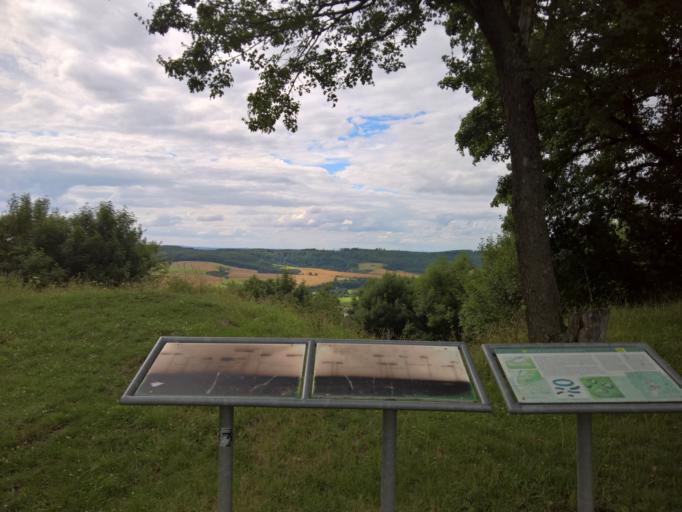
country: DE
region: Hesse
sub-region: Regierungsbezirk Darmstadt
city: Glauburg
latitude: 50.3110
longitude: 9.0126
